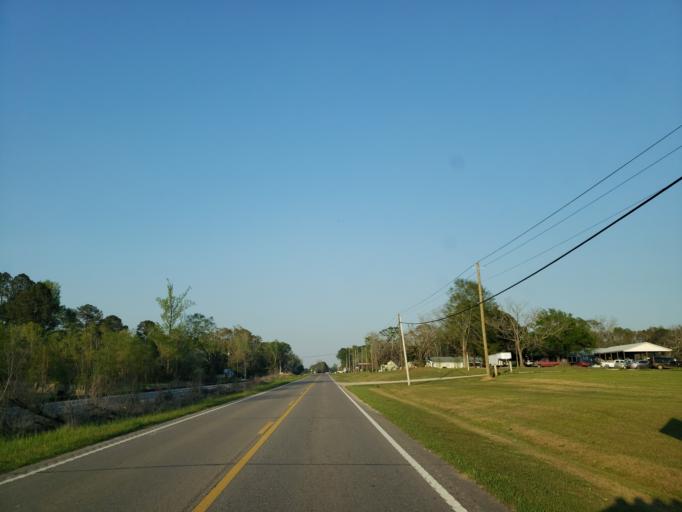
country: US
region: Mississippi
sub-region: Lauderdale County
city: Marion
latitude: 32.3998
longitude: -88.6033
